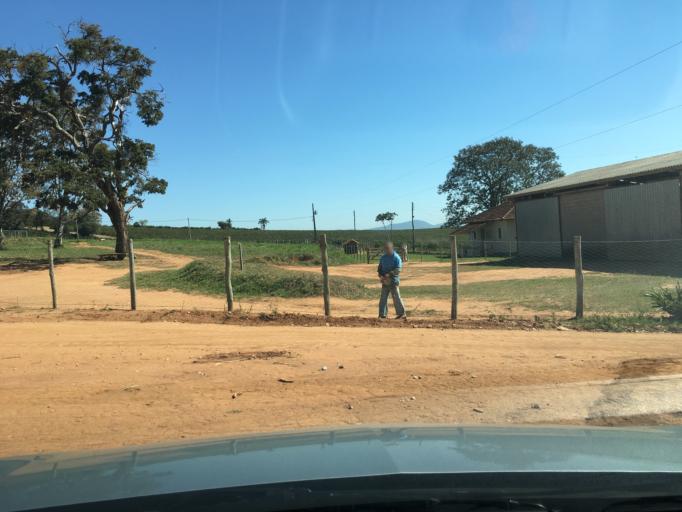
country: BR
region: Minas Gerais
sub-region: Campestre
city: Campestre
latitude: -21.5918
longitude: -46.2067
